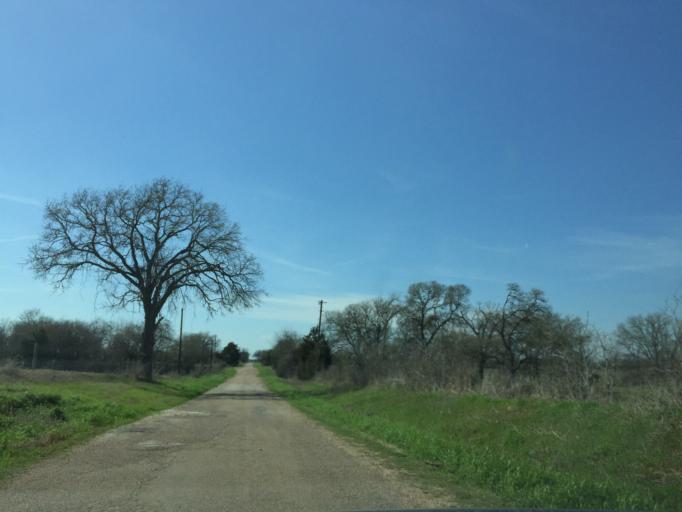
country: US
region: Texas
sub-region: Milam County
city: Thorndale
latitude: 30.5733
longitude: -97.1595
